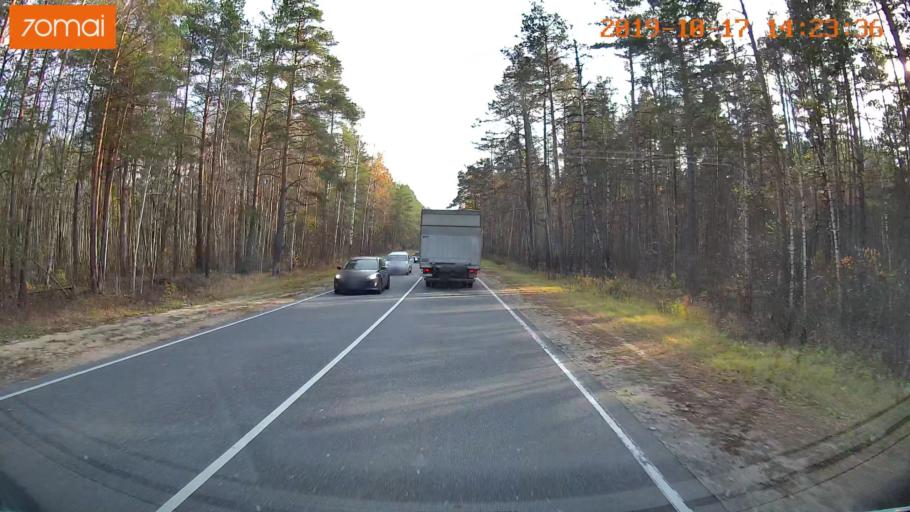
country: RU
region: Moskovskaya
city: Radovitskiy
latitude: 55.0171
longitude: 39.9614
